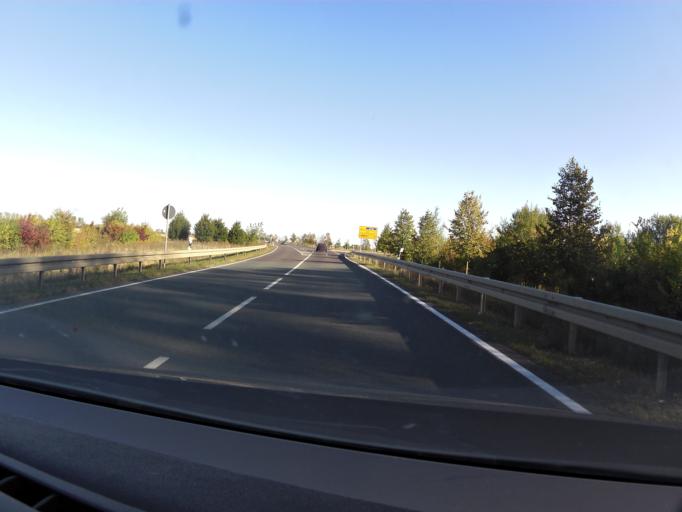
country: DE
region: Saxony-Anhalt
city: Kroppenstedt
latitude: 51.9412
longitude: 11.3272
